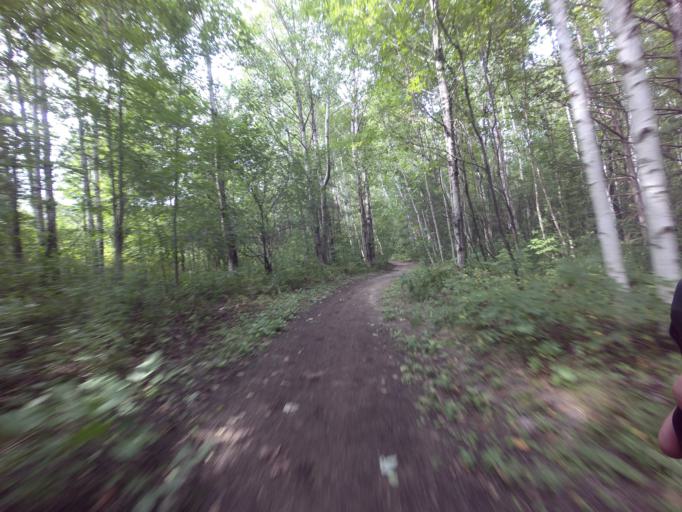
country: CA
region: Ontario
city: Bells Corners
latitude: 45.3194
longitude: -75.7982
